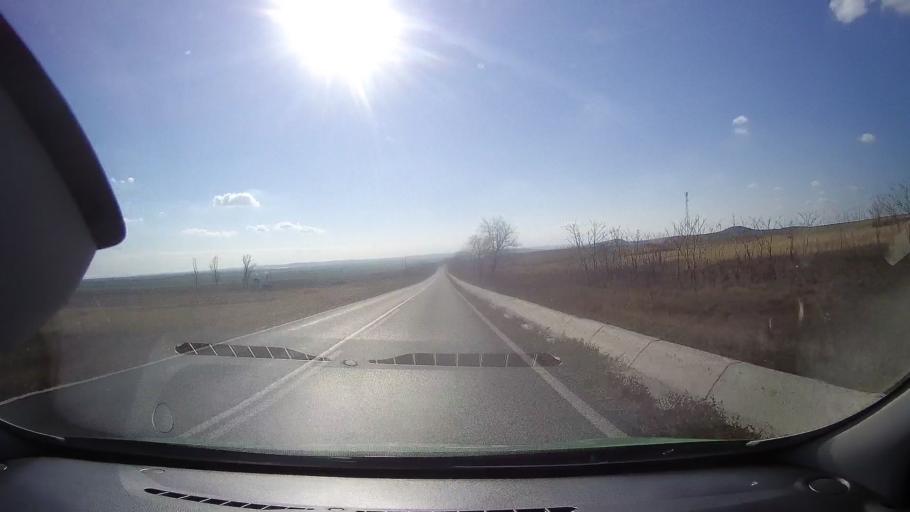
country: RO
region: Tulcea
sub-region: Comuna Ceamurlia de Jos
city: Ceamurlia de Jos
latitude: 44.8128
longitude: 28.6915
